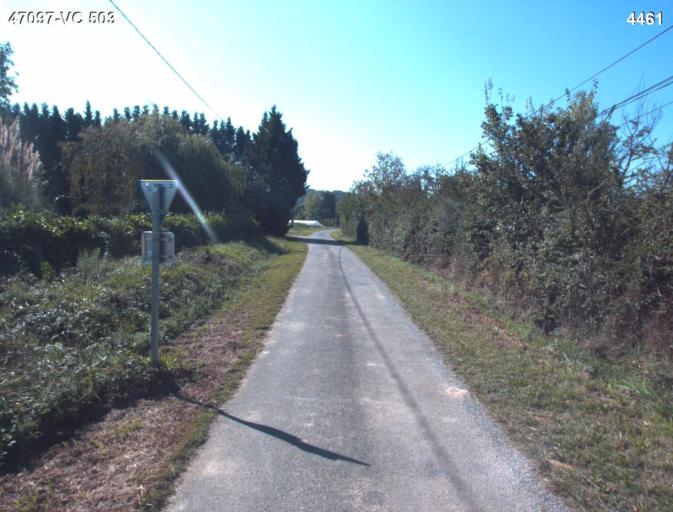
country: FR
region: Aquitaine
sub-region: Departement du Lot-et-Garonne
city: Port-Sainte-Marie
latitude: 44.2246
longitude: 0.3822
